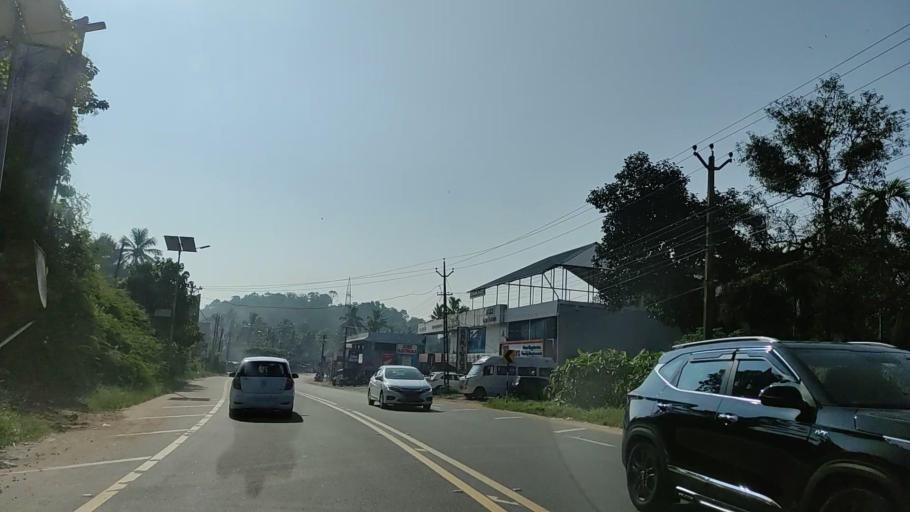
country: IN
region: Kerala
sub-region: Kollam
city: Punalur
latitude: 8.9064
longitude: 76.8545
